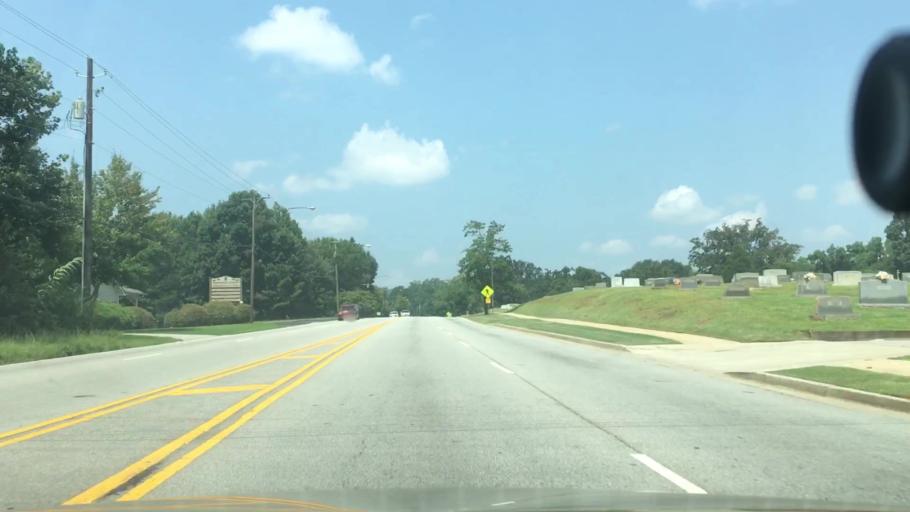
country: US
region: Georgia
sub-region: Spalding County
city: Griffin
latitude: 33.2436
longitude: -84.2508
